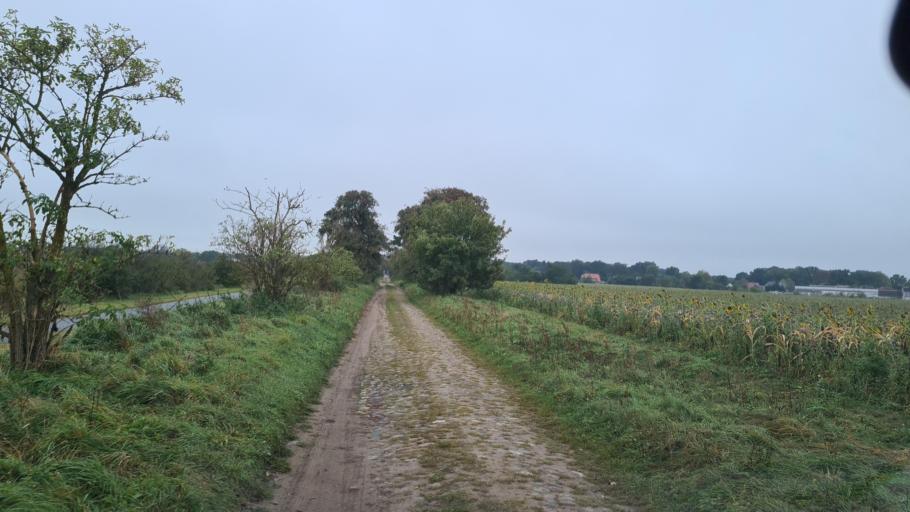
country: DE
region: Brandenburg
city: Furstenwalde
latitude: 52.4090
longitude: 14.0361
